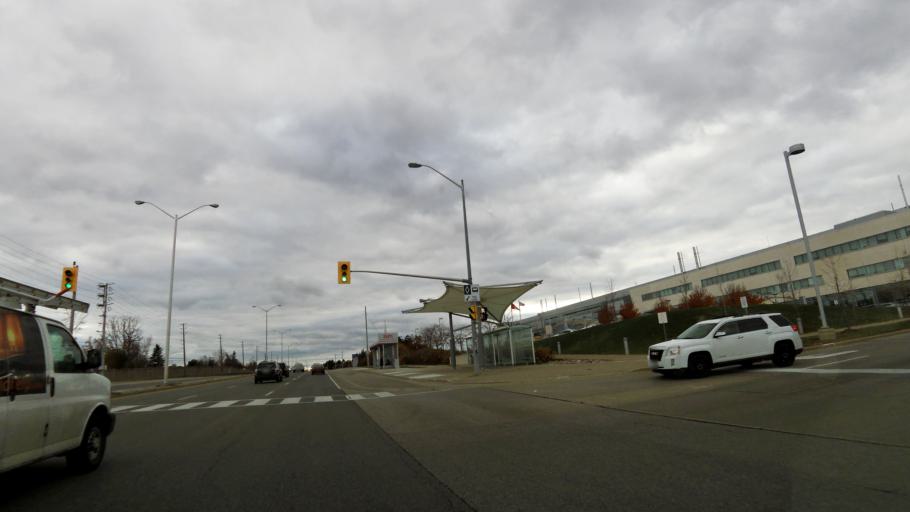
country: CA
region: Ontario
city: Brampton
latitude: 43.7474
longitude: -79.7411
